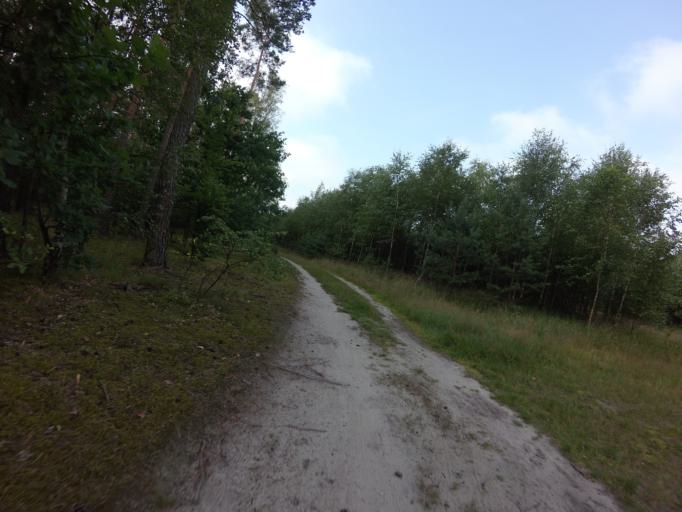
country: PL
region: Kujawsko-Pomorskie
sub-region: Powiat bydgoski
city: Osielsko
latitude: 53.1489
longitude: 18.0852
